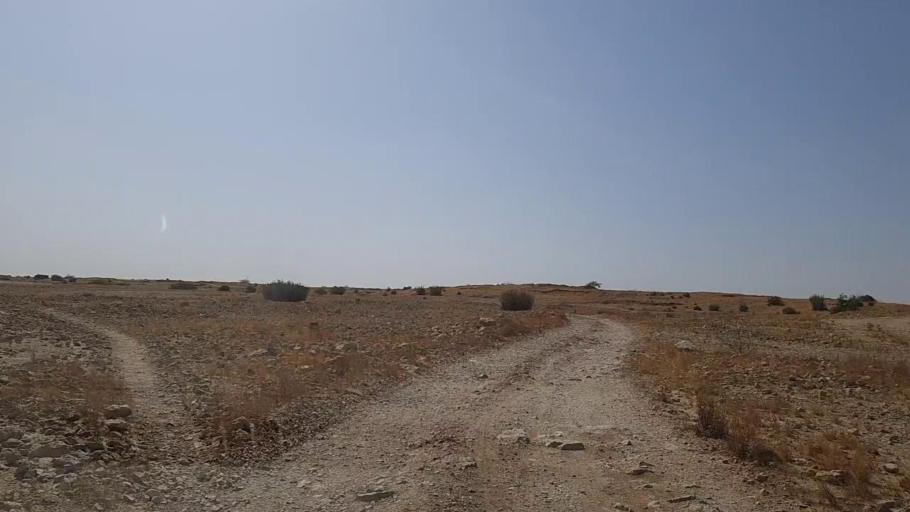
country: PK
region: Sindh
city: Kotri
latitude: 25.1651
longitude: 68.1887
